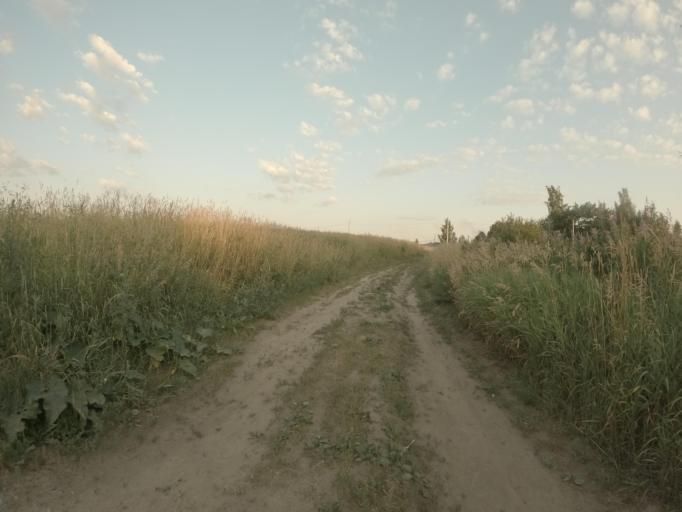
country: RU
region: Leningrad
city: Pavlovo
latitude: 59.8476
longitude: 30.9423
